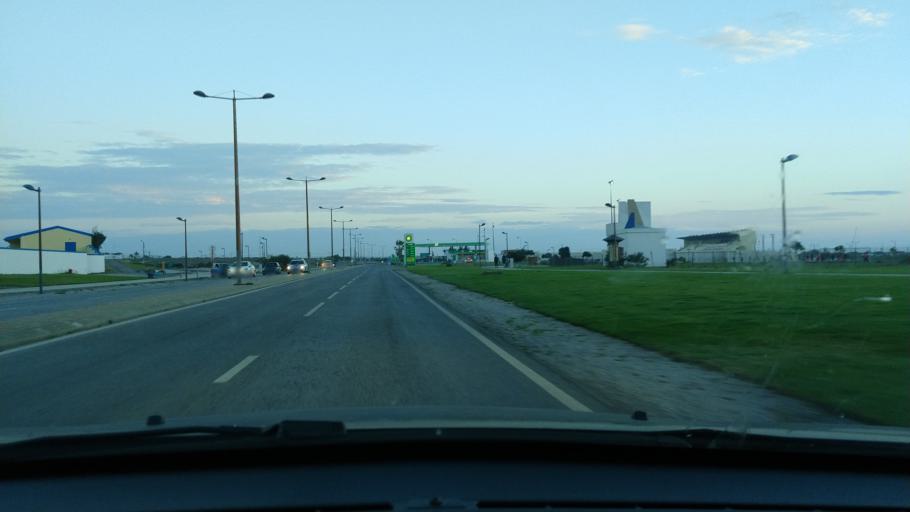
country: PT
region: Leiria
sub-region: Peniche
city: Peniche
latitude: 39.3551
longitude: -9.3633
